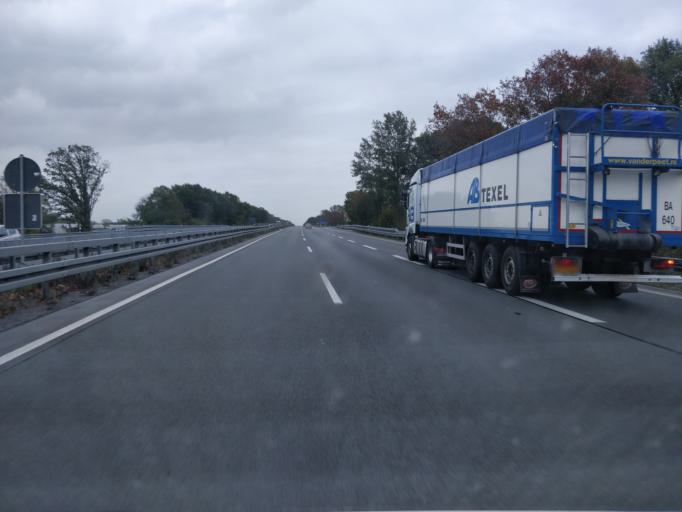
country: DE
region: North Rhine-Westphalia
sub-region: Regierungsbezirk Munster
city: Isselburg
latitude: 51.8175
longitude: 6.4398
